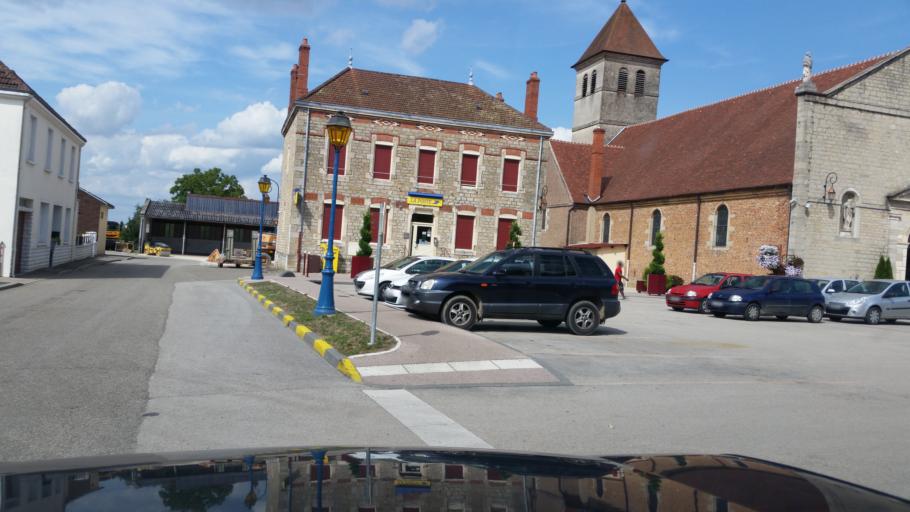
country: FR
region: Bourgogne
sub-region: Departement de Saone-et-Loire
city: Saint-Germain-du-Bois
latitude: 46.7531
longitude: 5.2418
